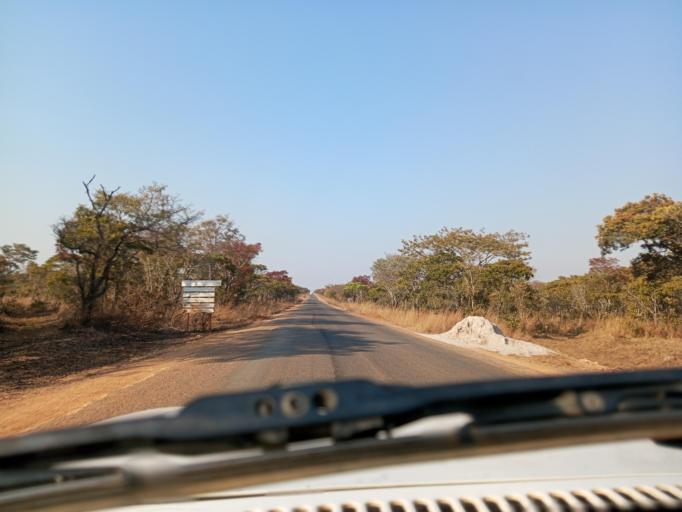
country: ZM
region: Northern
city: Mpika
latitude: -12.3992
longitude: 31.0894
